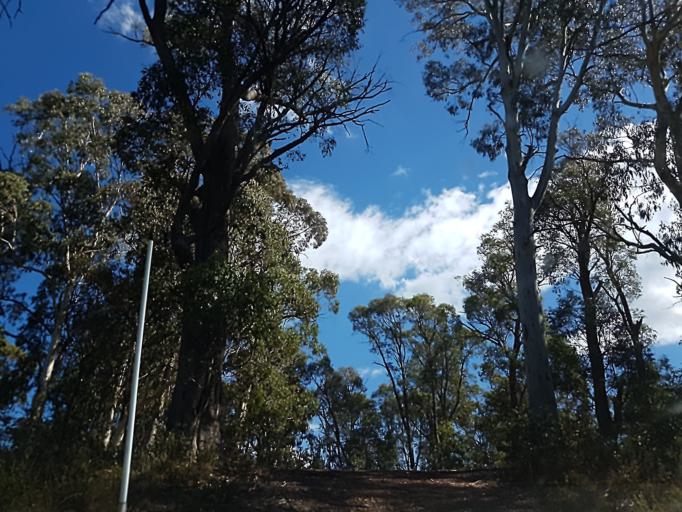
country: AU
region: Victoria
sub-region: Alpine
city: Mount Beauty
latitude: -36.8829
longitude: 147.0230
